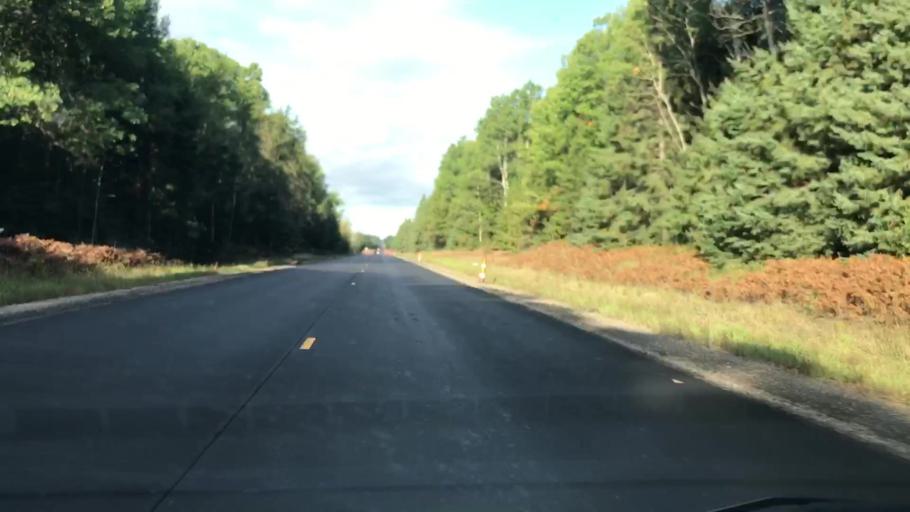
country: US
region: Michigan
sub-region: Mackinac County
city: Saint Ignace
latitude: 46.3459
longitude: -84.9395
